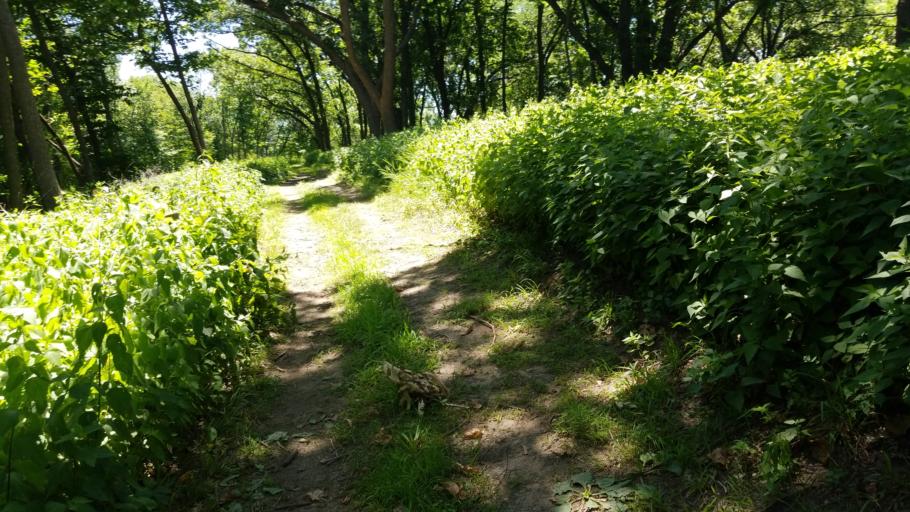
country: US
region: Iowa
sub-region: Pottawattamie County
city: Carter Lake
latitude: 41.3946
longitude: -95.9528
